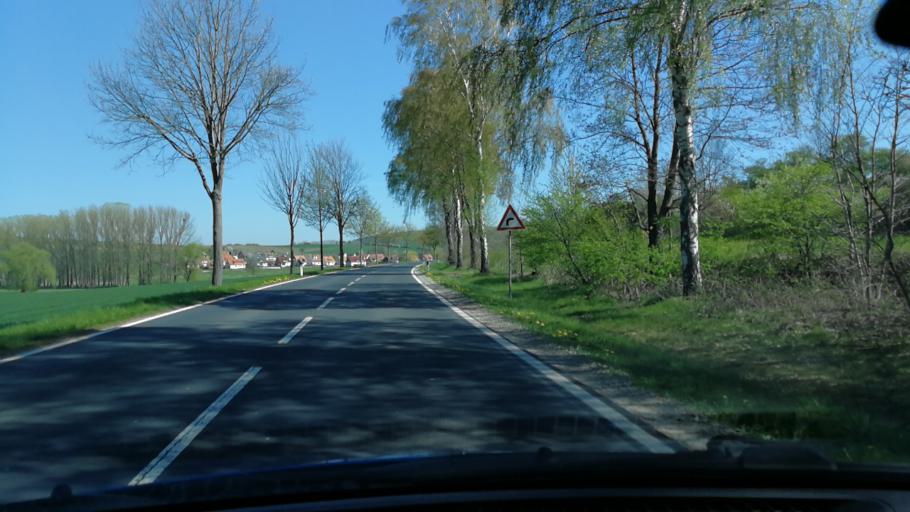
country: DE
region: Lower Saxony
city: Adelebsen
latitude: 51.5924
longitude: 9.7695
